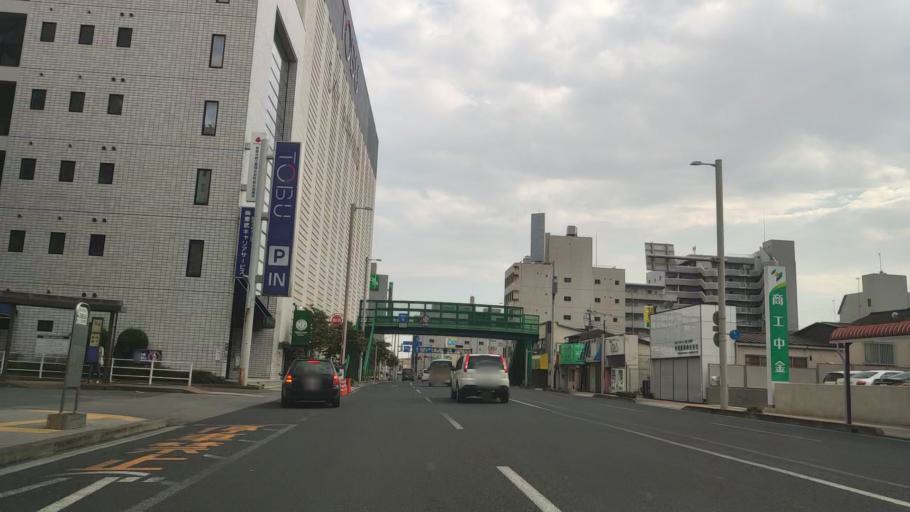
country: JP
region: Tochigi
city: Utsunomiya-shi
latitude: 36.5593
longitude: 139.8797
